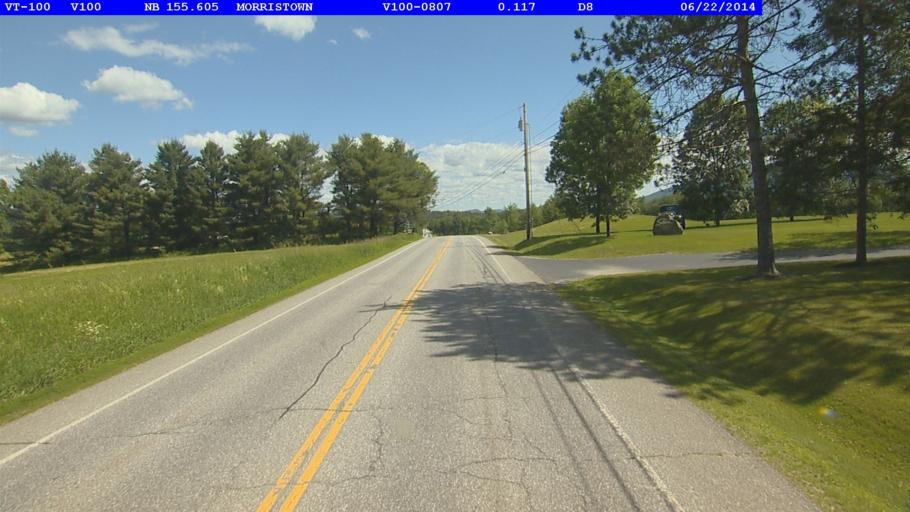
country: US
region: Vermont
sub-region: Lamoille County
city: Morristown
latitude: 44.4963
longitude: -72.6342
